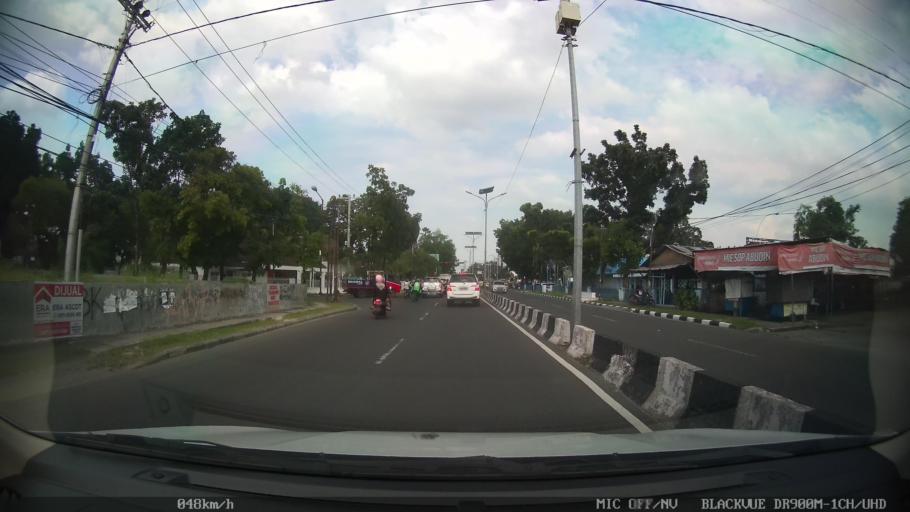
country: ID
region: North Sumatra
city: Medan
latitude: 3.5722
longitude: 98.6765
